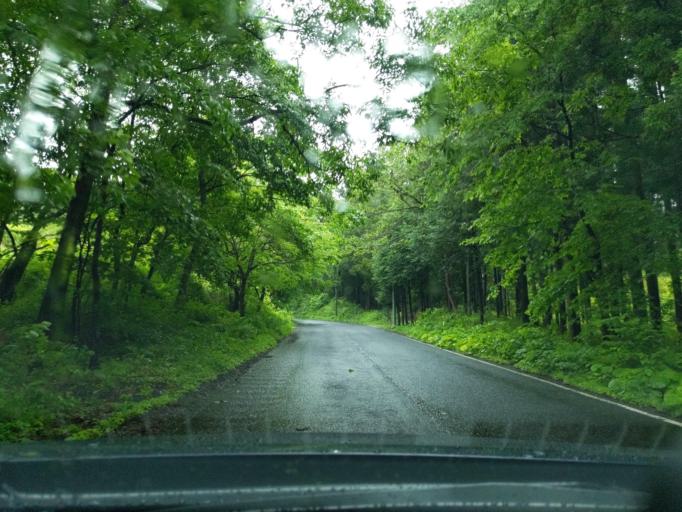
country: JP
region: Fukushima
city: Funehikimachi-funehiki
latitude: 37.6116
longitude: 140.6790
